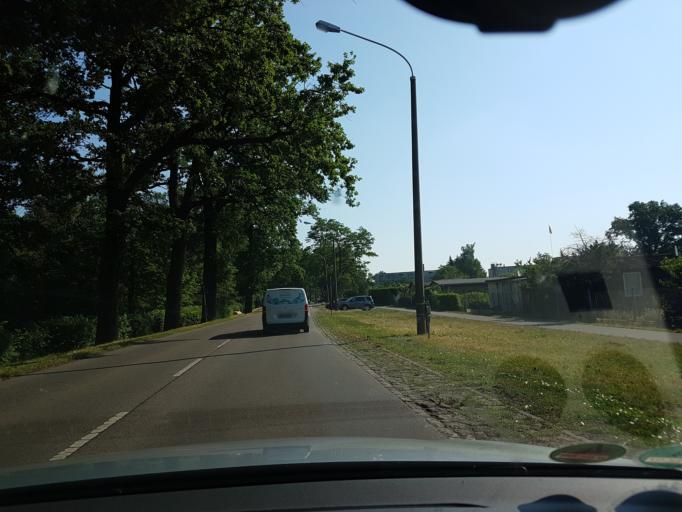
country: DE
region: Brandenburg
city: Brandenburg an der Havel
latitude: 52.3907
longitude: 12.5345
